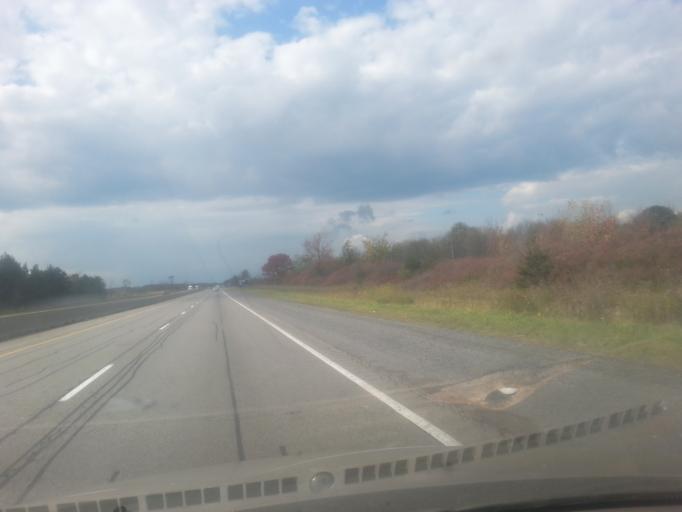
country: CA
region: Ontario
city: Kingston
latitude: 44.3109
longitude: -76.3931
